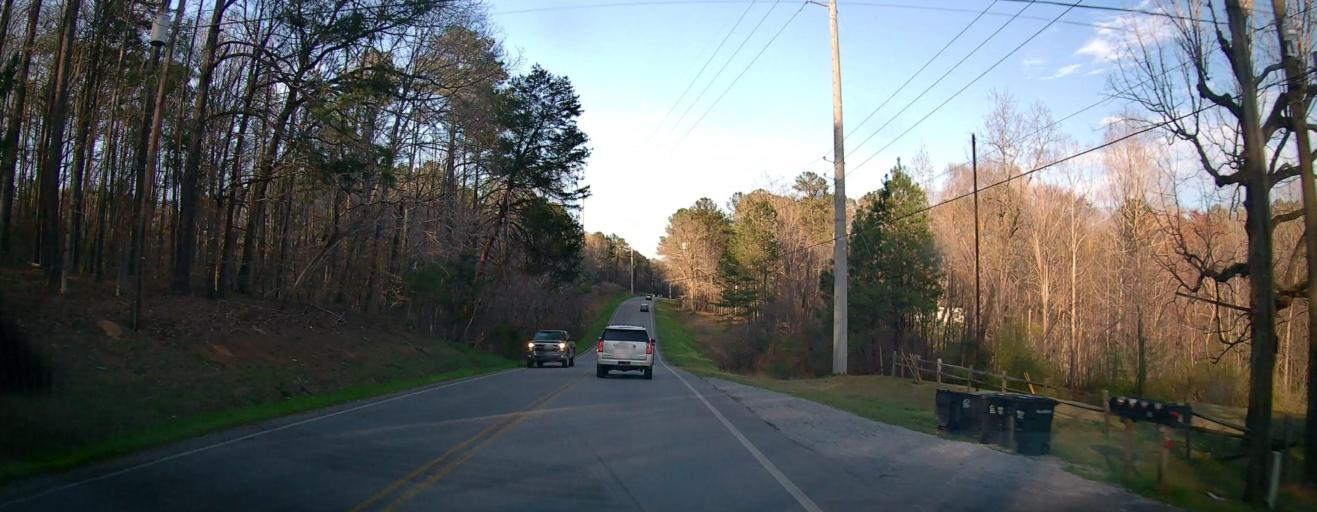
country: US
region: Alabama
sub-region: Shelby County
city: Indian Springs Village
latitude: 33.3119
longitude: -86.7330
